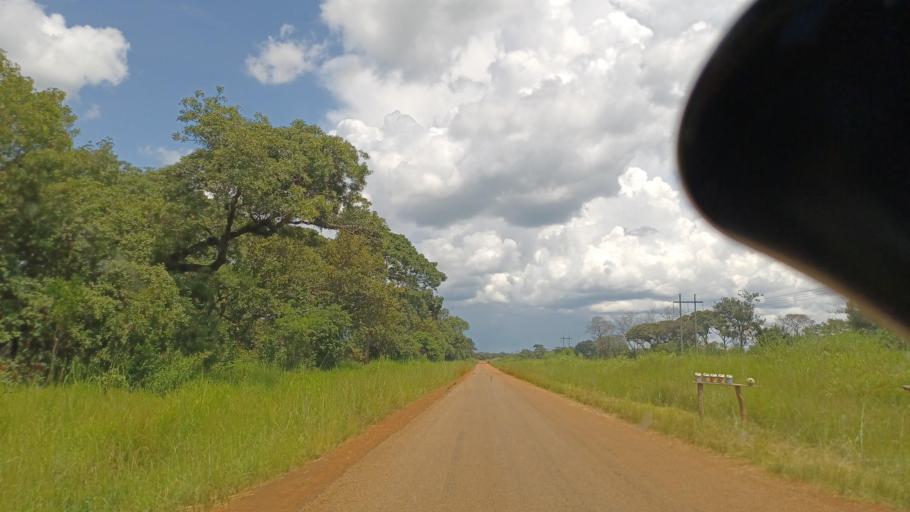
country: ZM
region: North-Western
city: Solwezi
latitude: -12.6851
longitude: 26.0406
